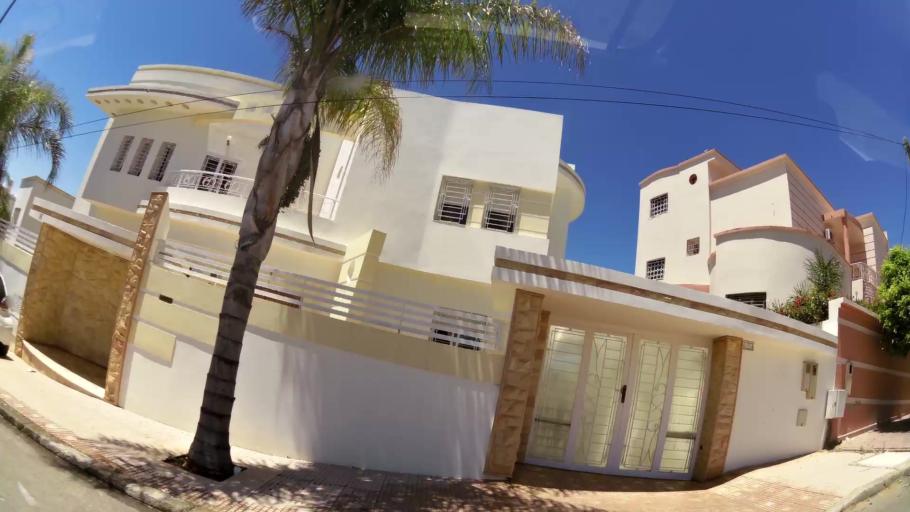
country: MA
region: Meknes-Tafilalet
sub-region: Meknes
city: Meknes
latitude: 33.9068
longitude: -5.5488
